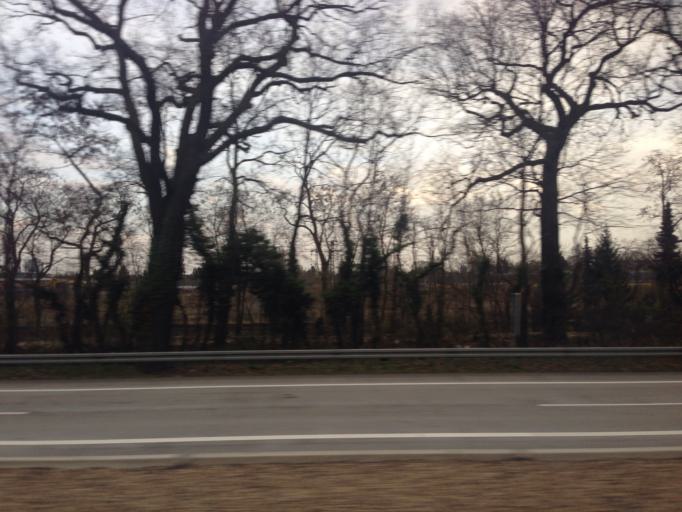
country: DE
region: Berlin
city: Grunewald
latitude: 52.4947
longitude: 13.2674
